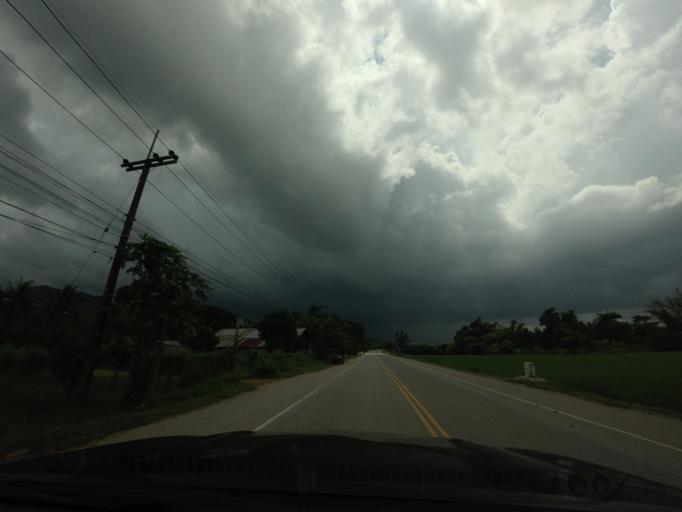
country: LA
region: Vientiane
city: Muang Sanakham
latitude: 17.9857
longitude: 101.7481
